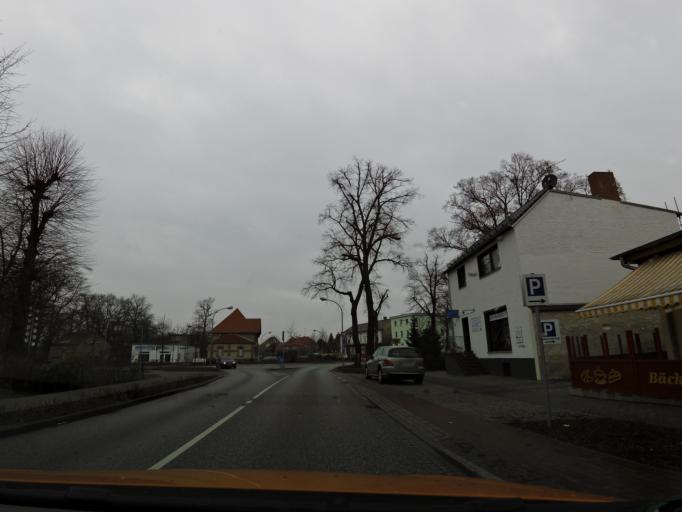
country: DE
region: Brandenburg
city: Gross Kreutz
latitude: 52.4035
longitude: 12.7774
